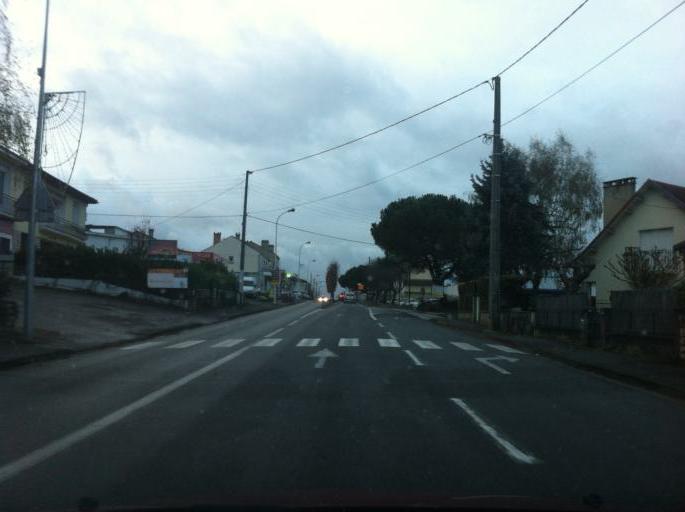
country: FR
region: Aquitaine
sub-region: Departement de la Dordogne
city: Perigueux
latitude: 45.1864
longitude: 0.6991
